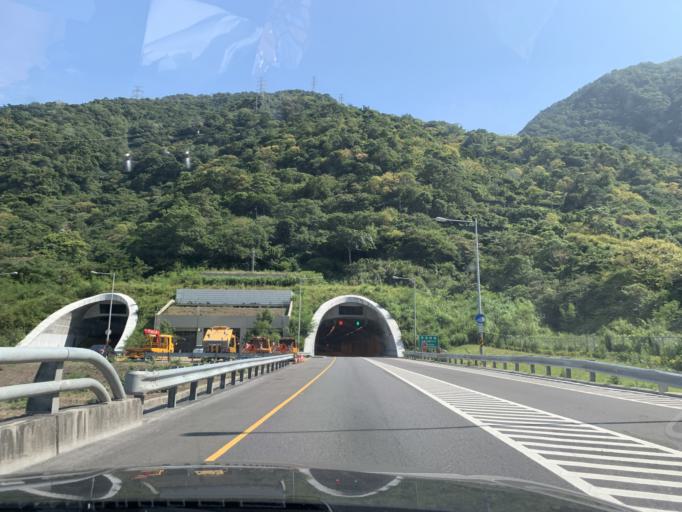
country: TW
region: Taiwan
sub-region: Yilan
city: Yilan
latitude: 24.5328
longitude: 121.8349
